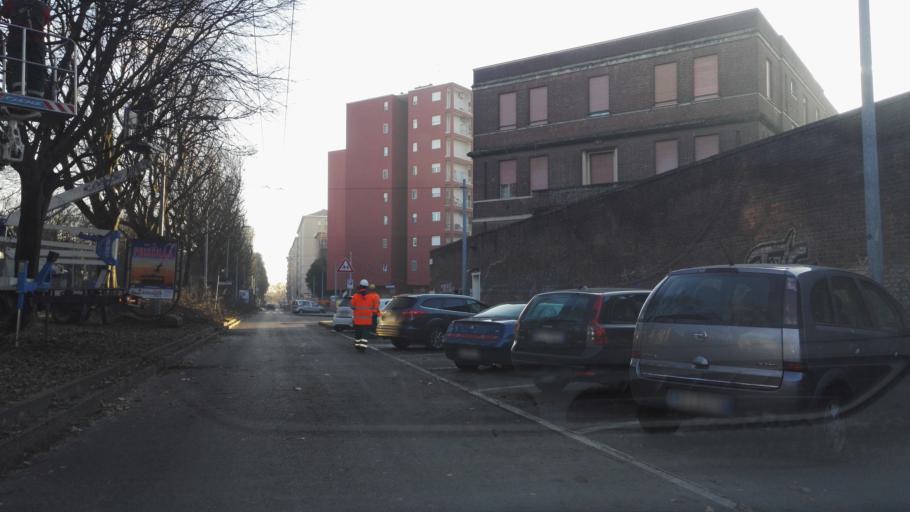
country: IT
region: Lombardy
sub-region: Citta metropolitana di Milano
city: Chiaravalle
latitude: 45.4367
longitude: 9.2241
